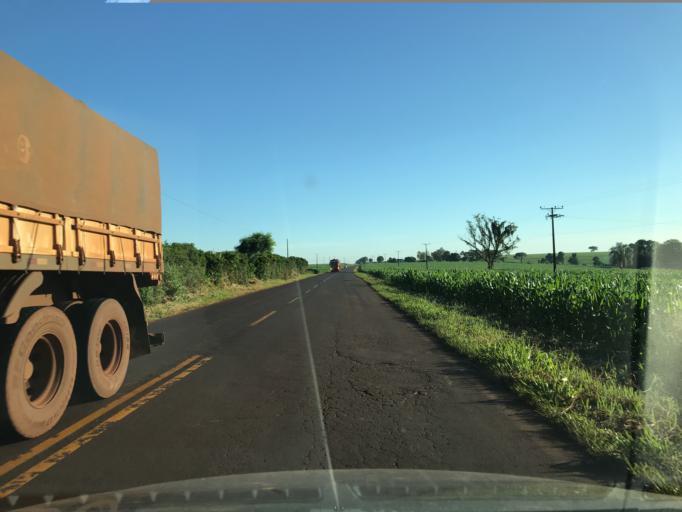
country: BR
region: Parana
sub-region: Palotina
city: Palotina
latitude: -24.1236
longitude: -53.8496
